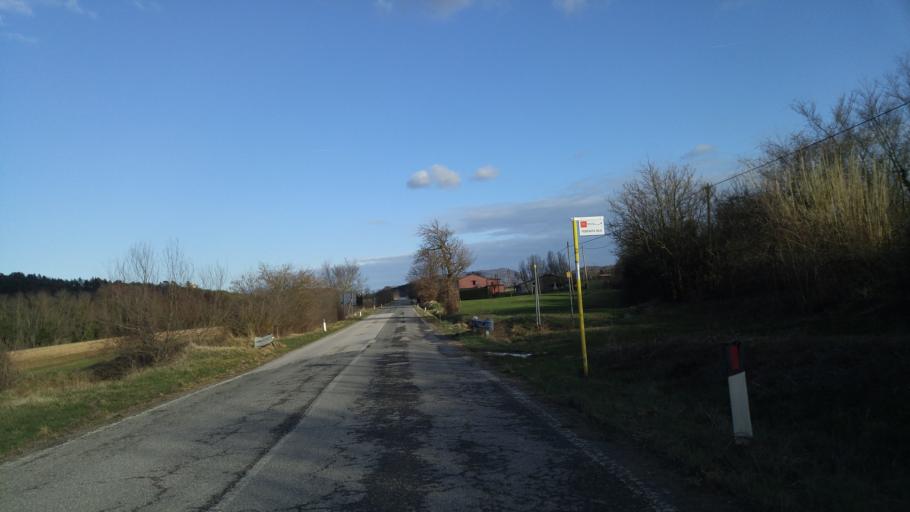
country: IT
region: The Marches
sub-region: Provincia di Pesaro e Urbino
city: Cagli
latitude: 43.5402
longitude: 12.6813
